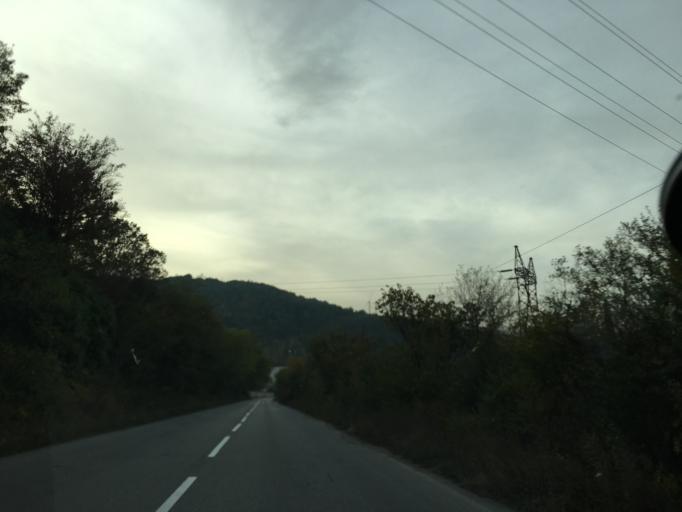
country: BG
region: Pazardzhik
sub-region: Obshtina Belovo
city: Belovo
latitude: 42.2313
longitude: 23.9544
